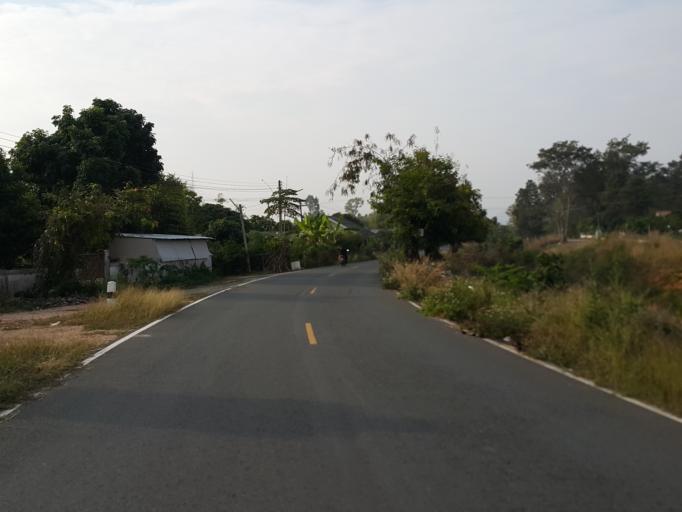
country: TH
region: Chiang Mai
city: San Sai
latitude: 18.8648
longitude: 99.1415
